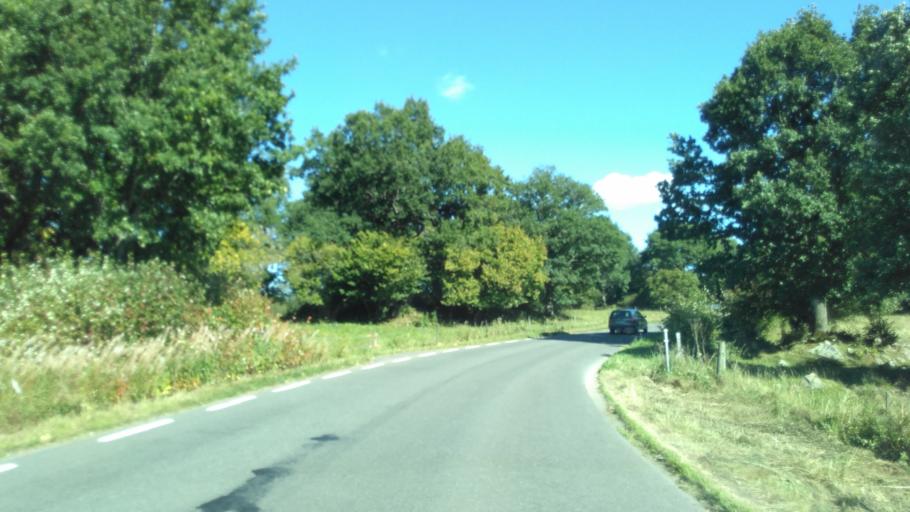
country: SE
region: Vaestra Goetaland
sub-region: Skara Kommun
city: Axvall
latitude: 58.4414
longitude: 13.6547
